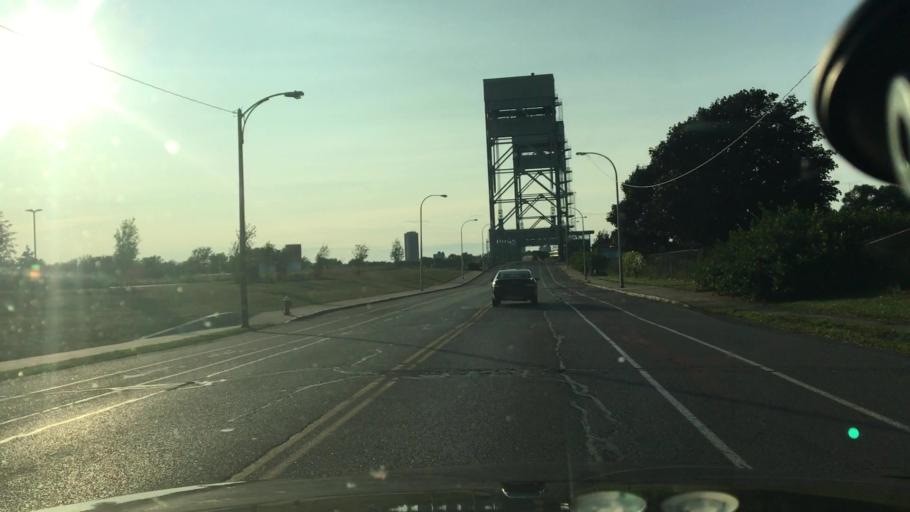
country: US
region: New York
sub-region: Erie County
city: Lackawanna
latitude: 42.8615
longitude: -78.8405
